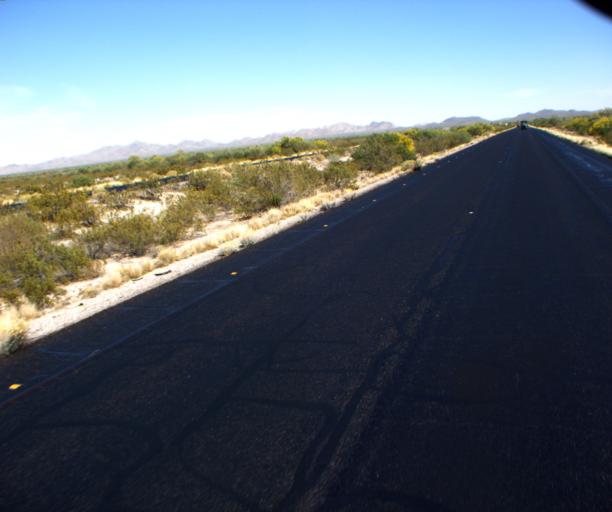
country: US
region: Arizona
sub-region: Pinal County
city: Maricopa
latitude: 32.8439
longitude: -112.2720
